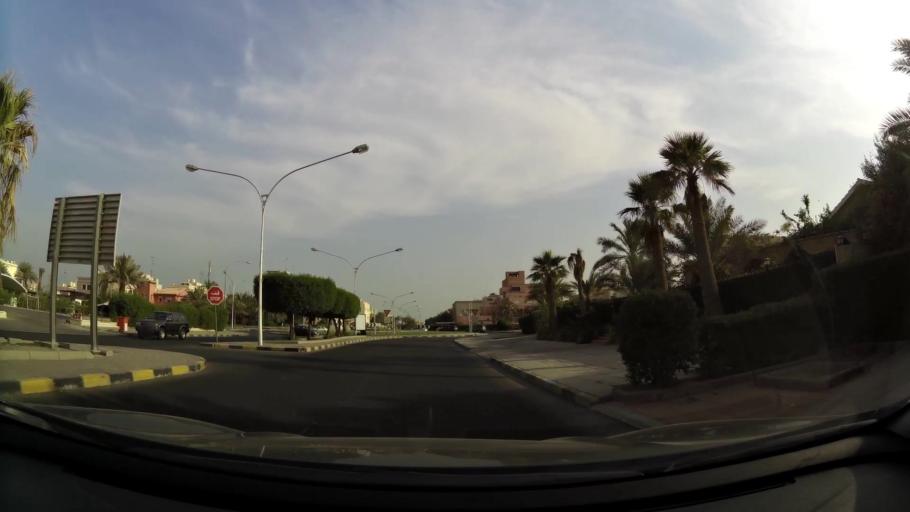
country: KW
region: Muhafazat Hawalli
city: Hawalli
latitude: 29.3156
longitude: 48.0095
